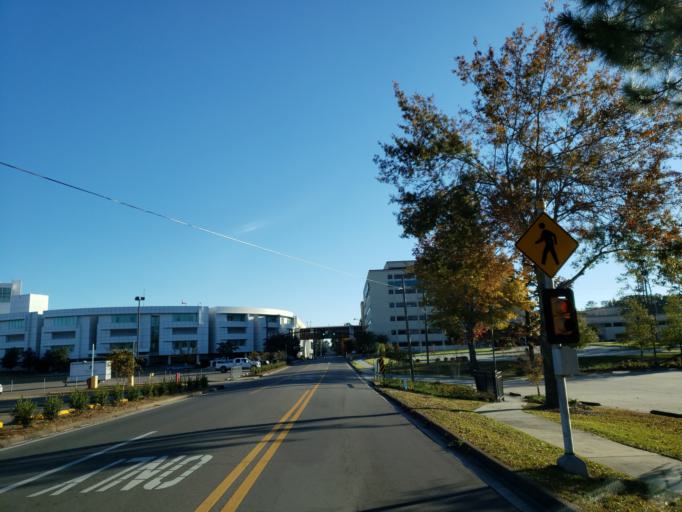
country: US
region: Mississippi
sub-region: Forrest County
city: Hattiesburg
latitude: 31.3207
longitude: -89.3313
